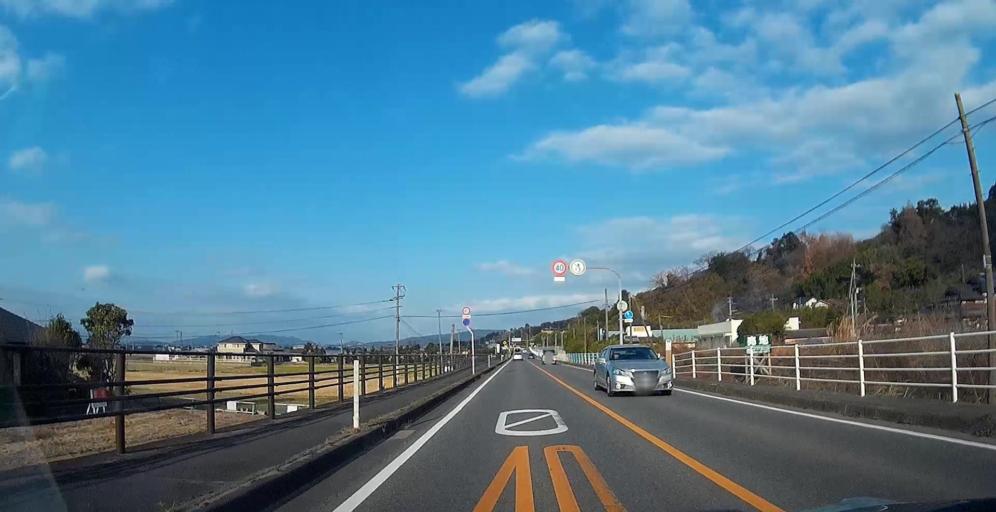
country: JP
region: Kumamoto
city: Matsubase
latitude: 32.5643
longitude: 130.6872
